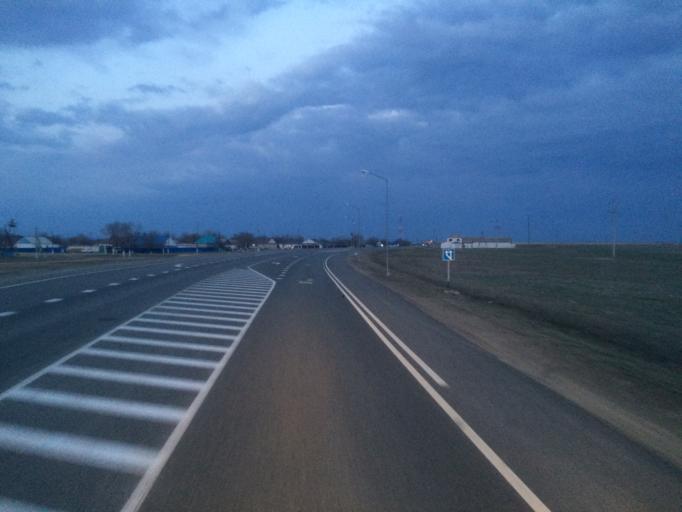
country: KZ
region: Aqtoebe
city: Martuk
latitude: 50.6400
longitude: 56.6882
